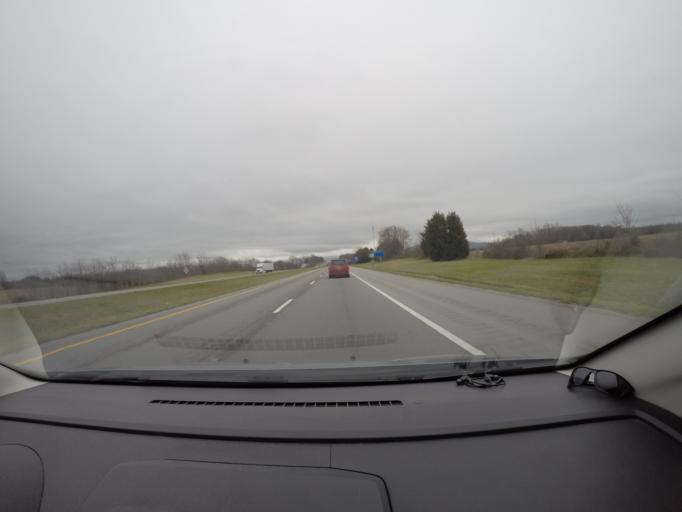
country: US
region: Tennessee
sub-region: Marion County
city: Monteagle
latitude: 35.3174
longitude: -85.9194
